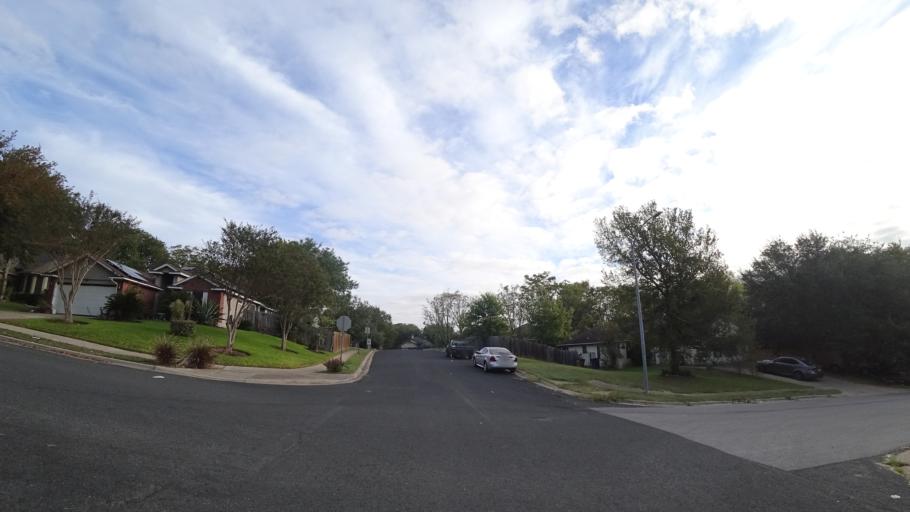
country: US
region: Texas
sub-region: Travis County
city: Onion Creek
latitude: 30.1914
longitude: -97.7324
